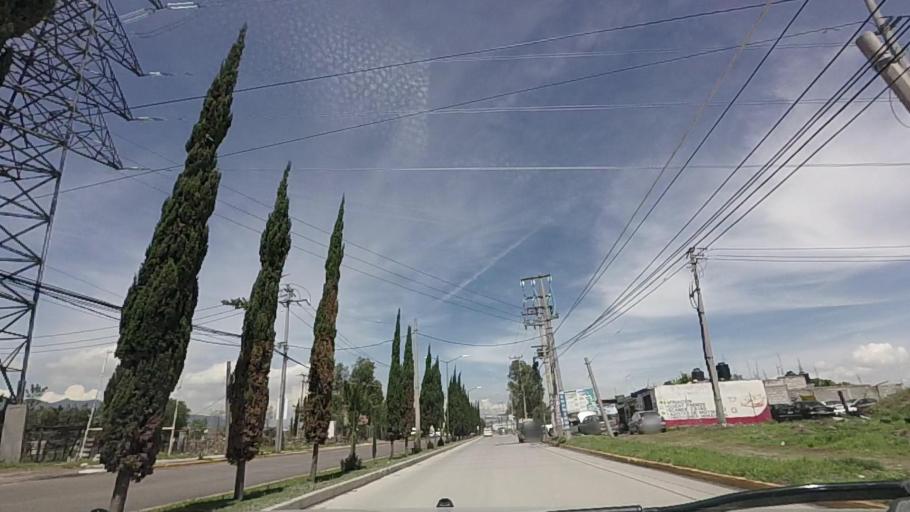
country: MX
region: Mexico
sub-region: Huehuetoca
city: Colonia Santa Teresa
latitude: 19.8297
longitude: -99.2298
